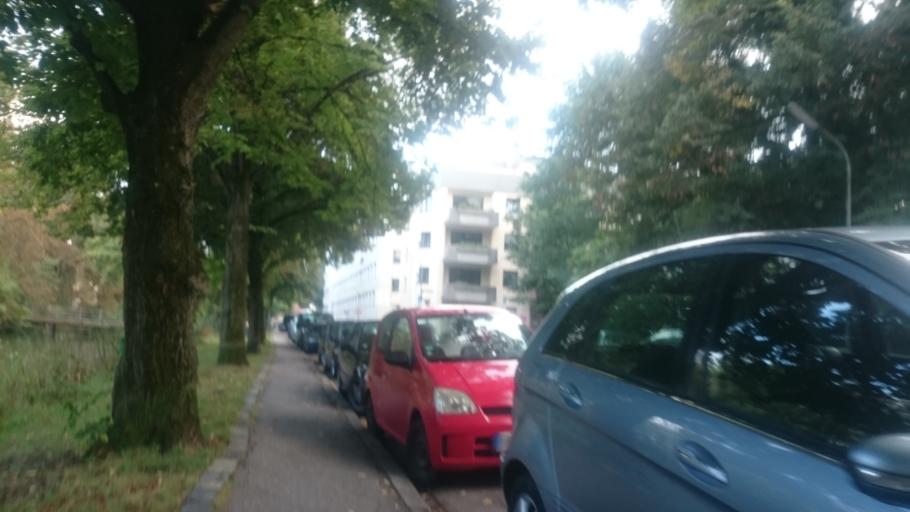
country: DE
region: Bavaria
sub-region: Swabia
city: Augsburg
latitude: 48.3732
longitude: 10.9073
